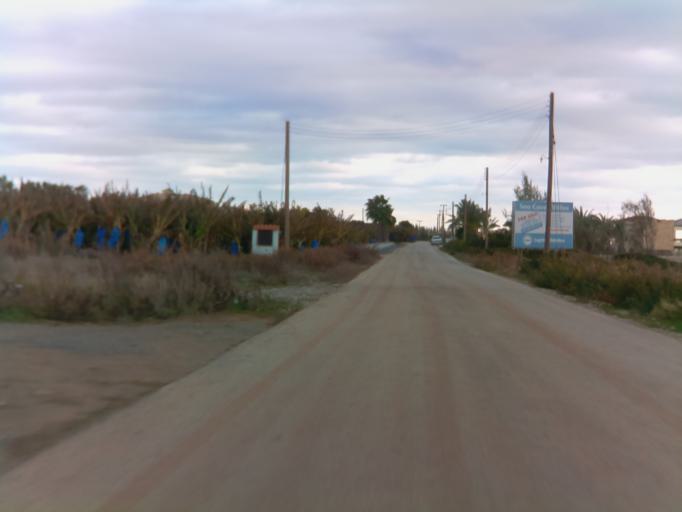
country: CY
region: Pafos
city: Pegeia
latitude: 34.8830
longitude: 32.3333
